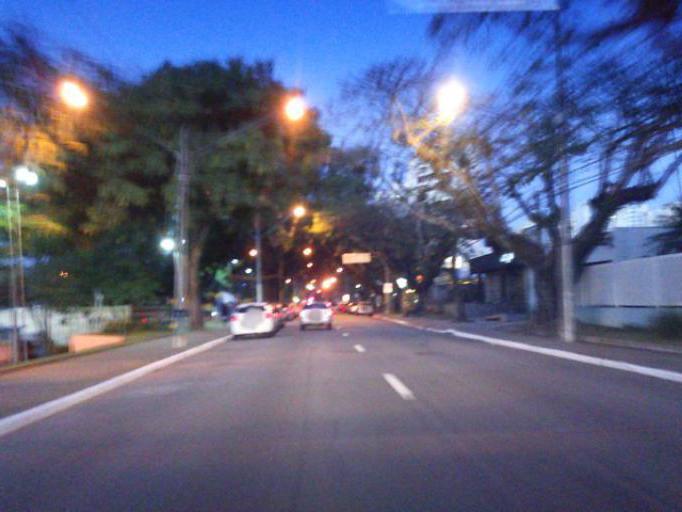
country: BR
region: Sao Paulo
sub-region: Sao Jose Dos Campos
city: Sao Jose dos Campos
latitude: -23.1927
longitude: -45.8963
